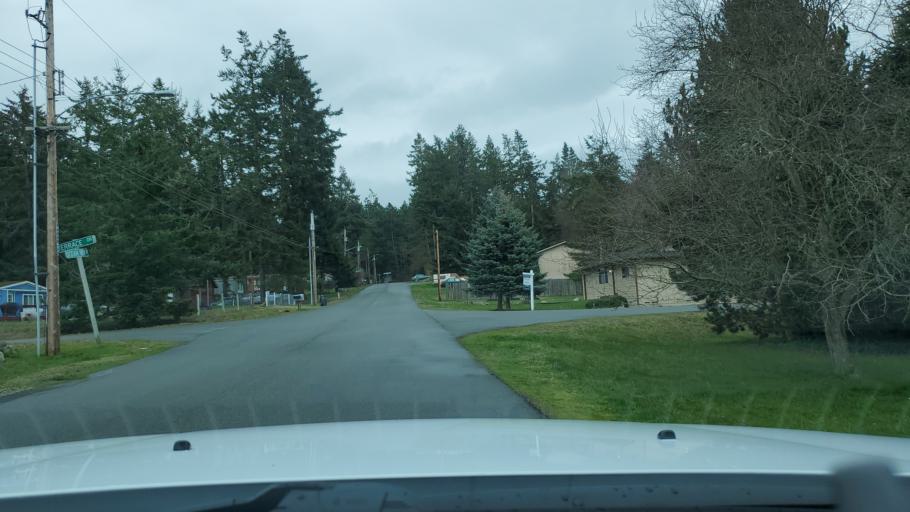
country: US
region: Washington
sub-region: Island County
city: Ault Field
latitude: 48.3689
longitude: -122.6457
